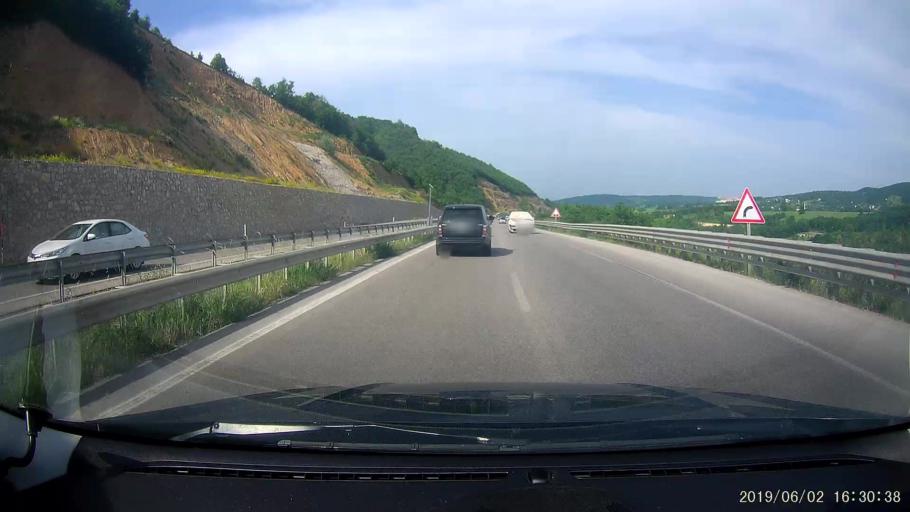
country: TR
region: Samsun
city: Ladik
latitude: 41.0269
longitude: 35.8863
